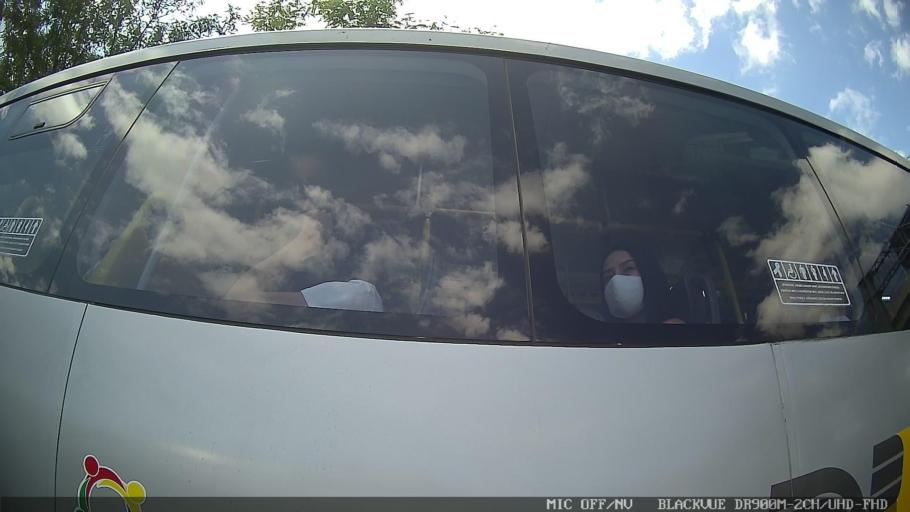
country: BR
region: Sao Paulo
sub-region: Ferraz De Vasconcelos
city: Ferraz de Vasconcelos
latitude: -23.5435
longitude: -46.4640
